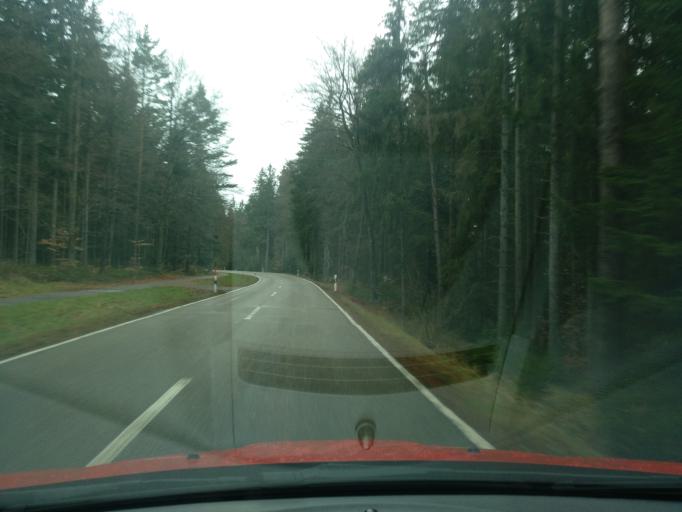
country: DE
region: Baden-Wuerttemberg
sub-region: Freiburg Region
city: Sankt Georgen im Schwarzwald
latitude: 48.1331
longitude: 8.3183
